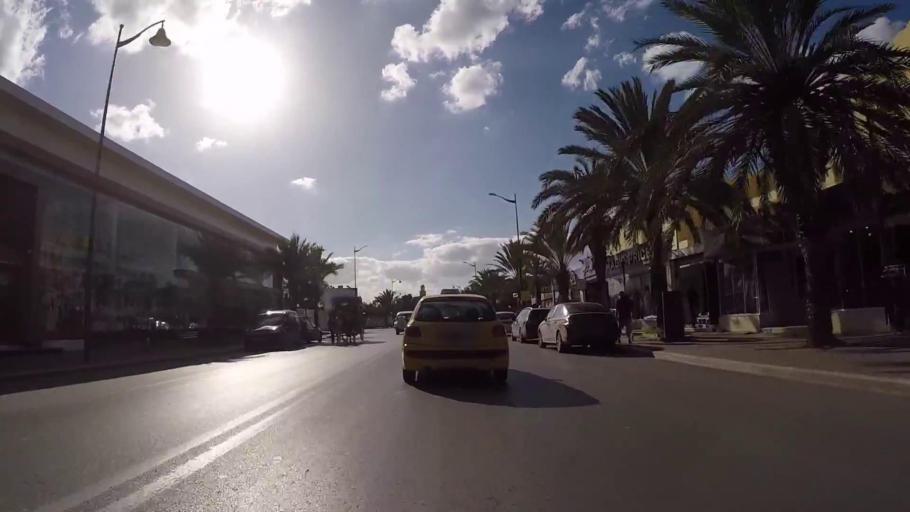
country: TN
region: Nabul
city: Al Hammamat
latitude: 36.3717
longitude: 10.5389
